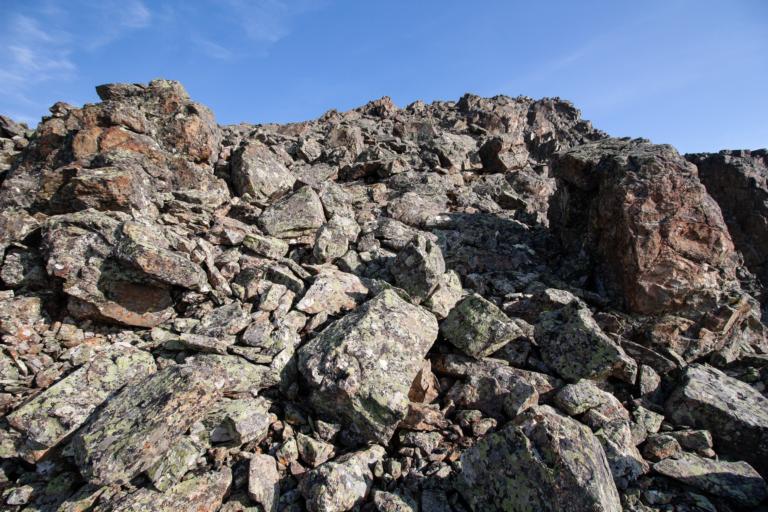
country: RU
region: Respublika Buryatiya
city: Kichera
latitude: 56.3645
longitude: 110.0786
